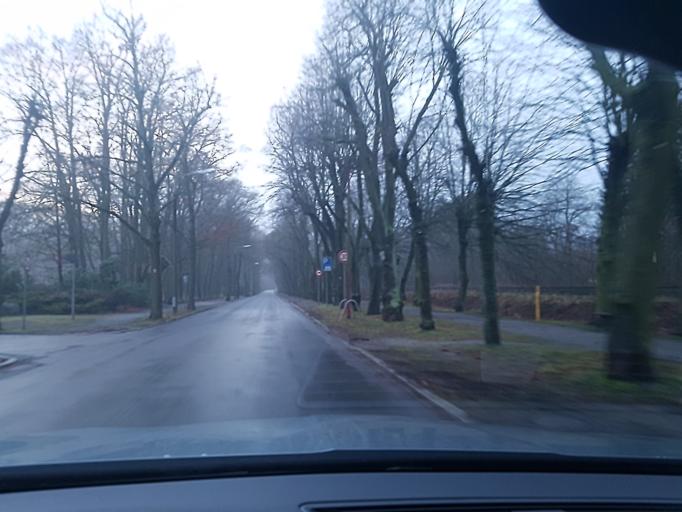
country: DE
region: Brandenburg
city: Finsterwalde
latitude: 51.6330
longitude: 13.6947
